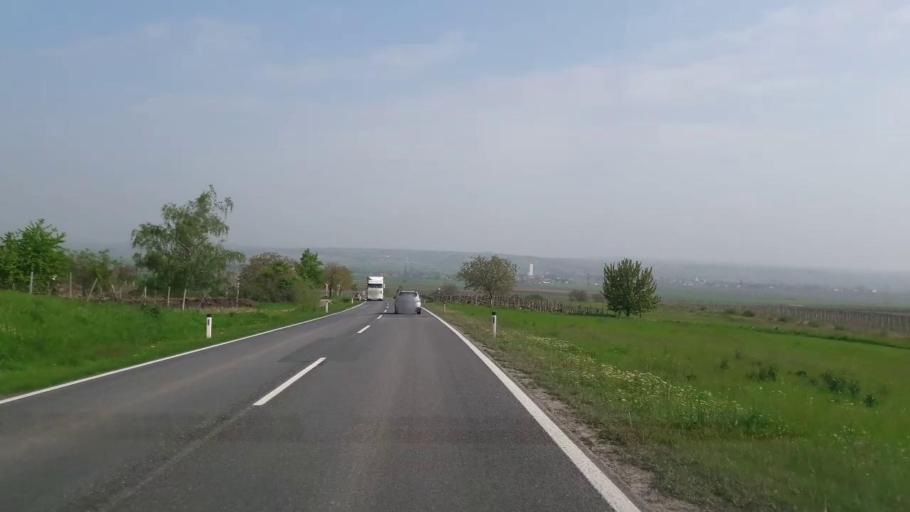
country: AT
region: Lower Austria
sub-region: Politischer Bezirk Hollabrunn
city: Haugsdorf
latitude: 48.6839
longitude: 16.0585
